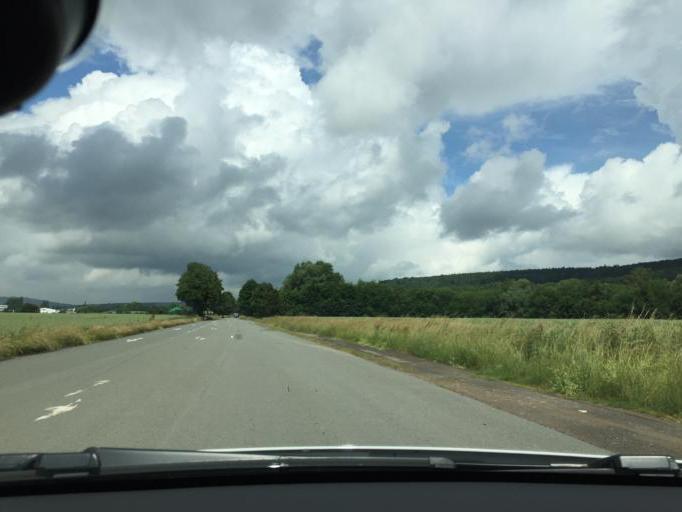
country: DE
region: Lower Saxony
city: Hehlen
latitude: 52.0372
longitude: 9.4102
